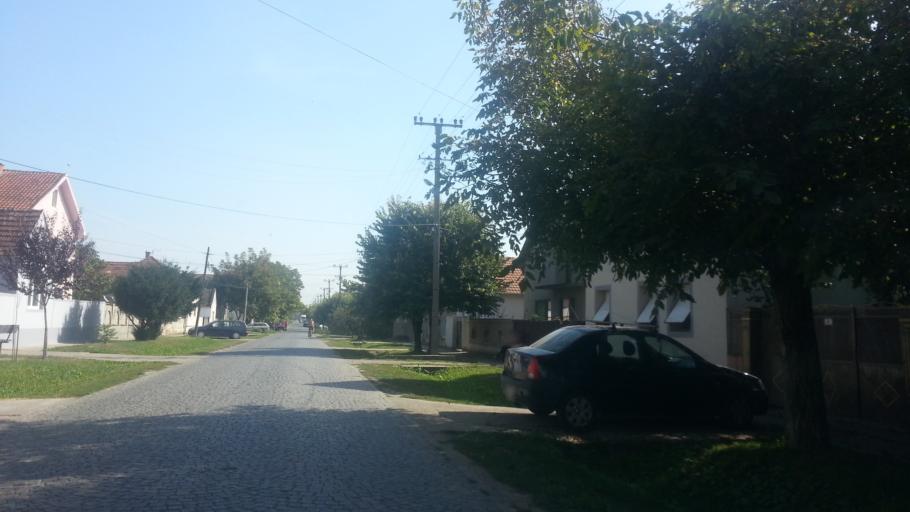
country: RS
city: Stari Banovci
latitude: 44.9940
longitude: 20.2845
